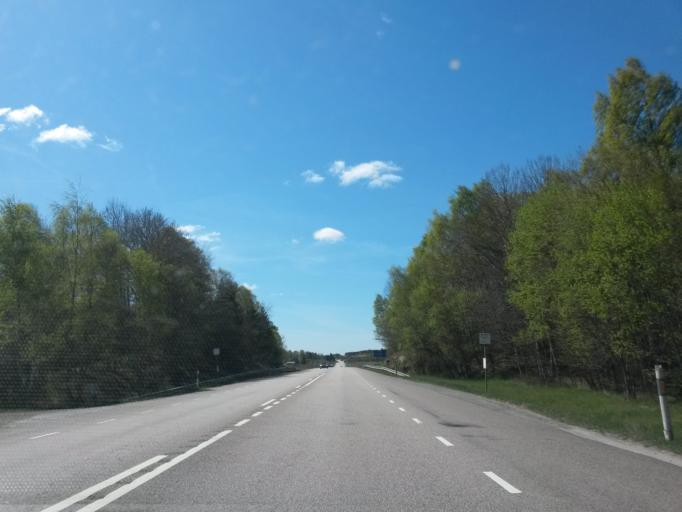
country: SE
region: Vaestra Goetaland
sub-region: Alingsas Kommun
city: Alingsas
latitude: 57.9623
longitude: 12.6202
